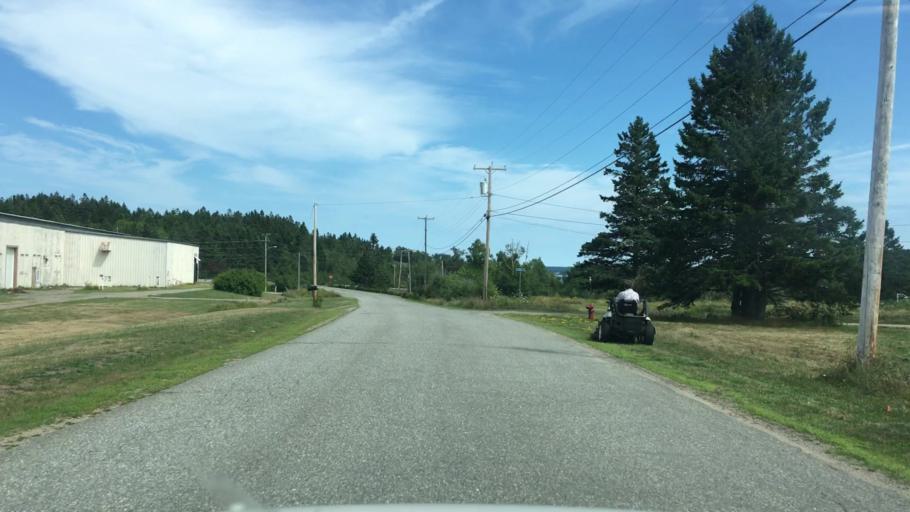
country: US
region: Maine
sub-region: Washington County
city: Eastport
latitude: 44.9269
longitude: -67.0269
